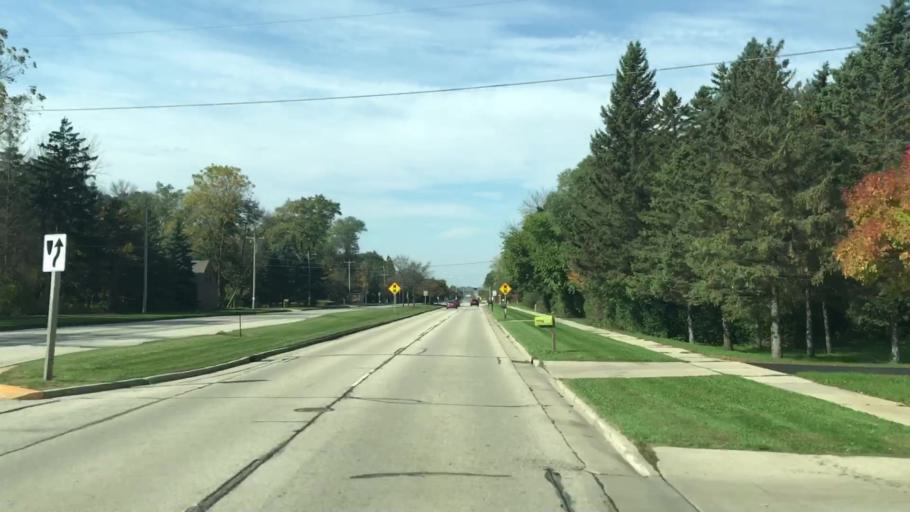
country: US
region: Wisconsin
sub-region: Ozaukee County
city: Thiensville
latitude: 43.2216
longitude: -87.9601
